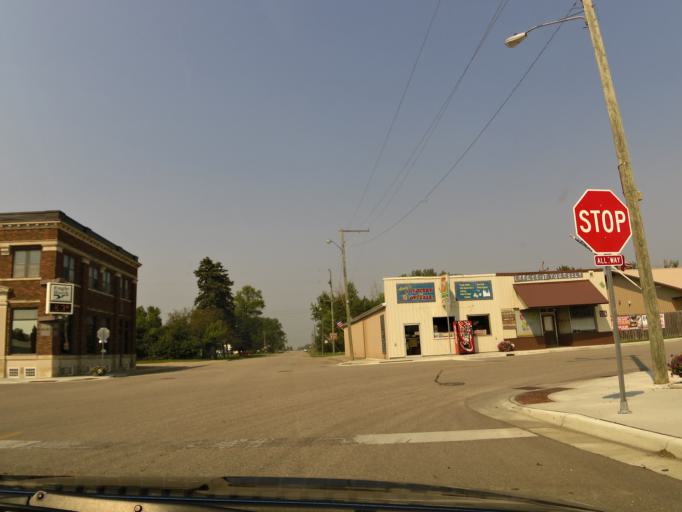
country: US
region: Minnesota
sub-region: Grant County
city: Elbow Lake
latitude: 46.0358
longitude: -96.1007
